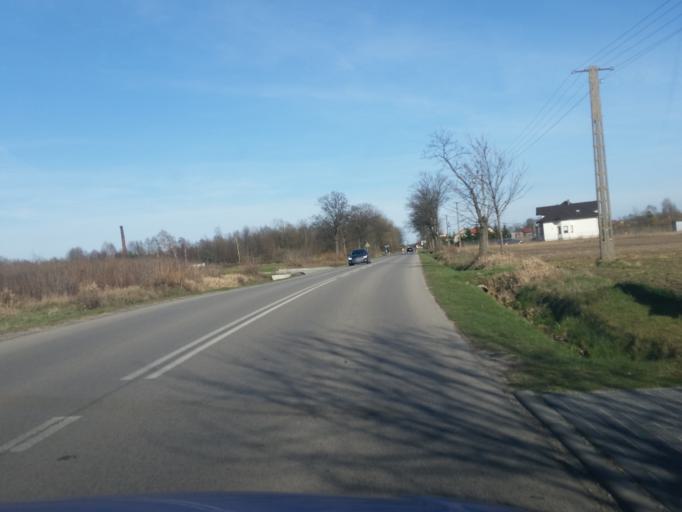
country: PL
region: Lodz Voivodeship
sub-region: Powiat radomszczanski
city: Kamiensk
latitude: 51.2078
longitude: 19.5321
